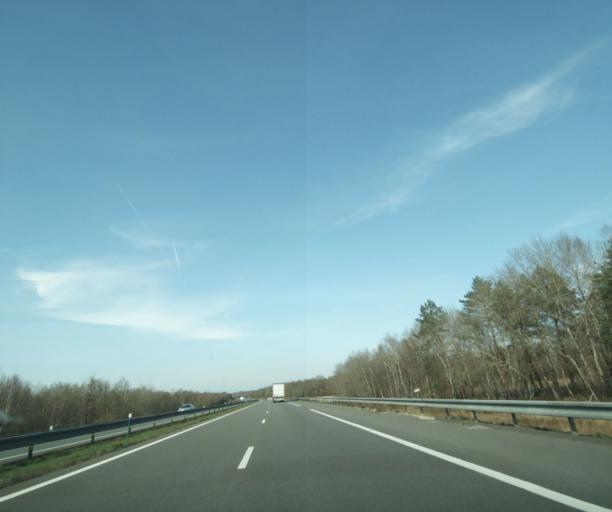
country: FR
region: Centre
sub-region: Departement du Loir-et-Cher
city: Theillay
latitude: 47.3635
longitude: 2.0531
